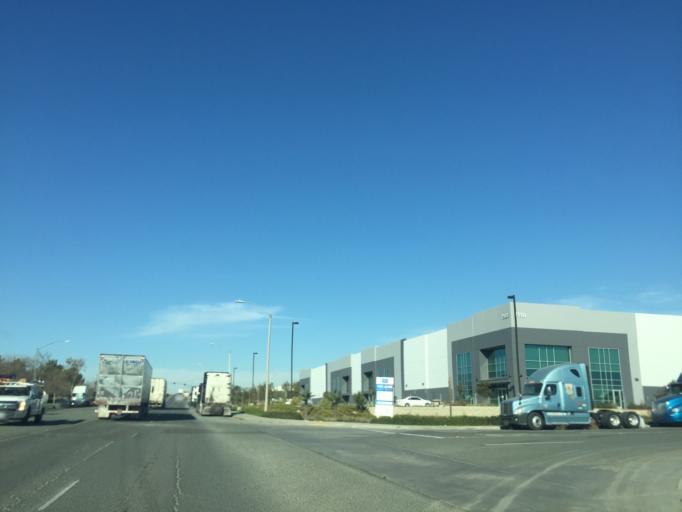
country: MX
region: Baja California
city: Tijuana
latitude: 32.5582
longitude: -116.9278
